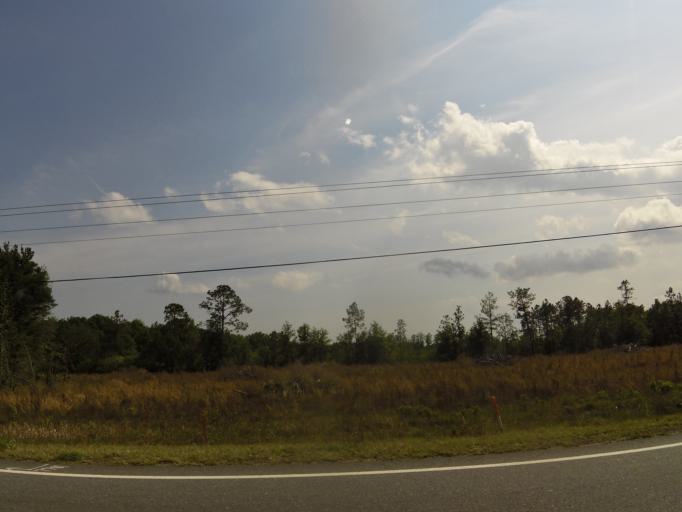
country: US
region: Georgia
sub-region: Camden County
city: Kingsland
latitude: 30.8095
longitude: -81.7935
